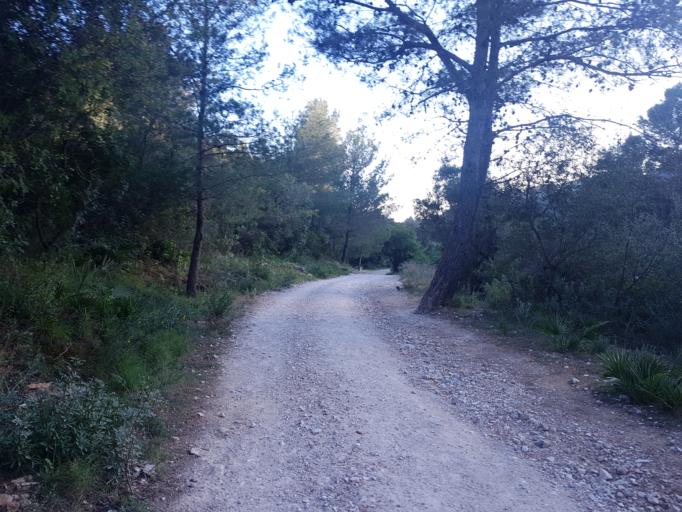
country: ES
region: Andalusia
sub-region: Provincia de Malaga
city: Marbella
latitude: 36.5375
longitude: -4.8841
